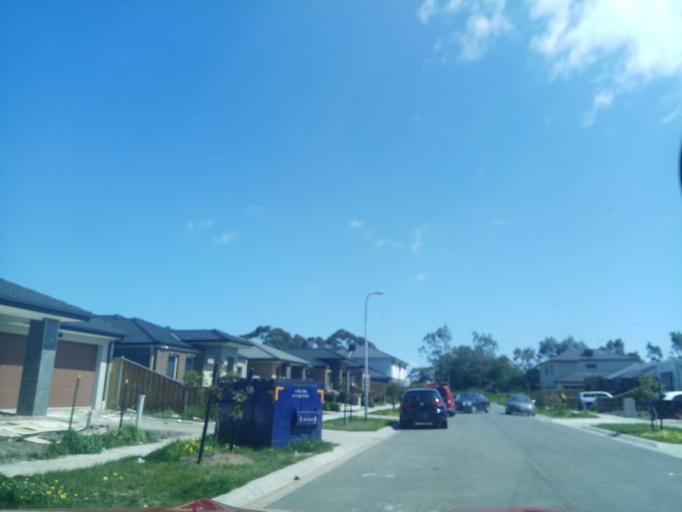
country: AU
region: Victoria
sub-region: Casey
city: Lynbrook
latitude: -38.0529
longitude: 145.2461
